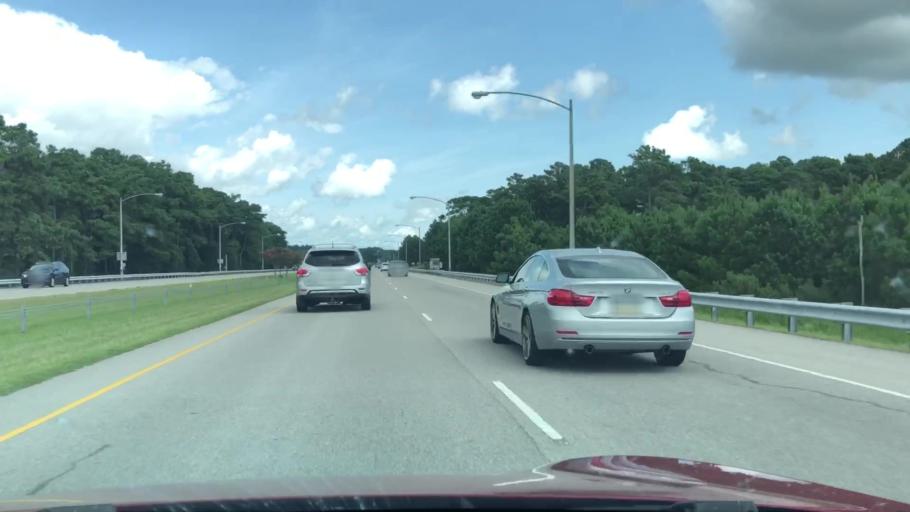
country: US
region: Virginia
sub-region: Northampton County
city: Cape Charles
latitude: 37.1259
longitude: -75.9679
